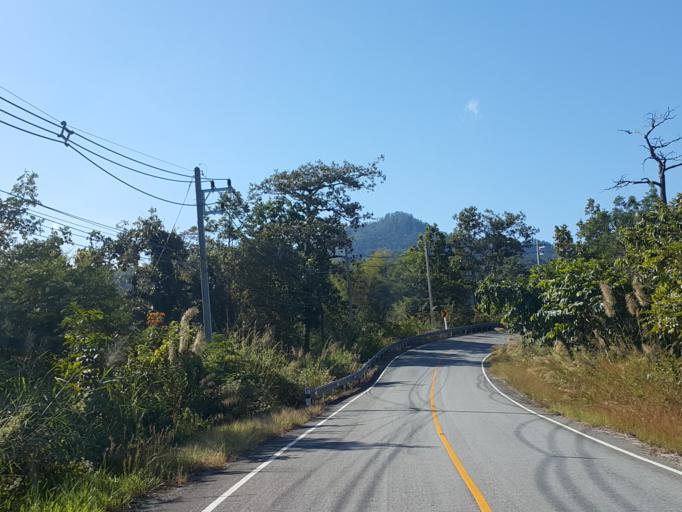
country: TH
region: Chiang Mai
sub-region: Amphoe Chiang Dao
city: Chiang Dao
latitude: 19.5269
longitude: 98.8877
